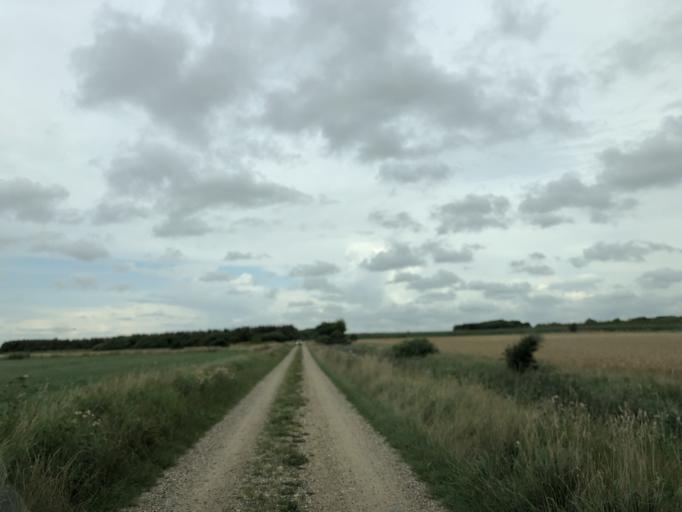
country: DK
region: Central Jutland
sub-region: Ringkobing-Skjern Kommune
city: Ringkobing
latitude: 56.1272
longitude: 8.2502
